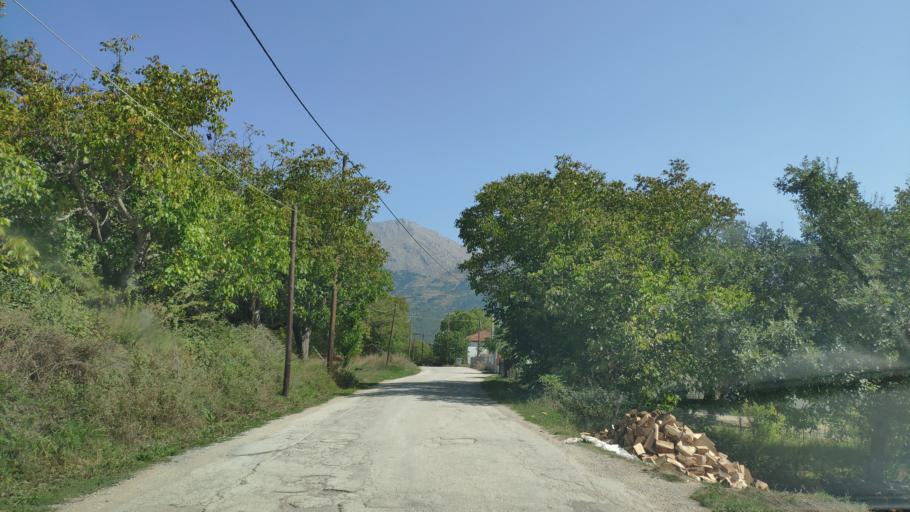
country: GR
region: West Greece
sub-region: Nomos Achaias
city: Kalavryta
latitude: 37.9129
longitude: 22.3030
